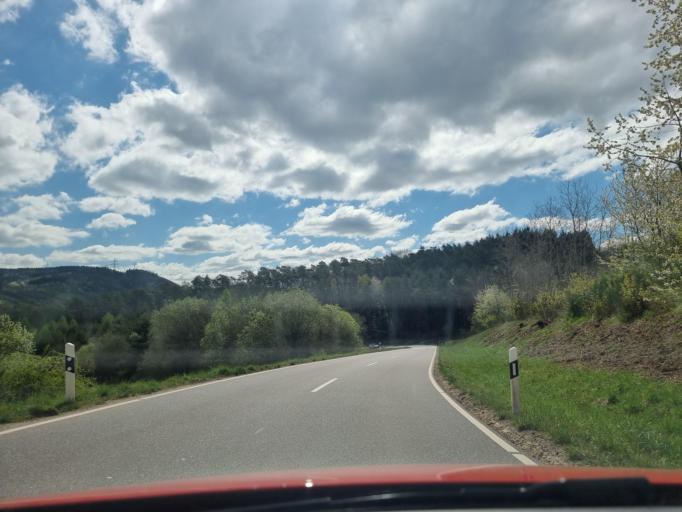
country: DE
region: Rheinland-Pfalz
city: Longuich
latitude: 49.7845
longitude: 6.7657
